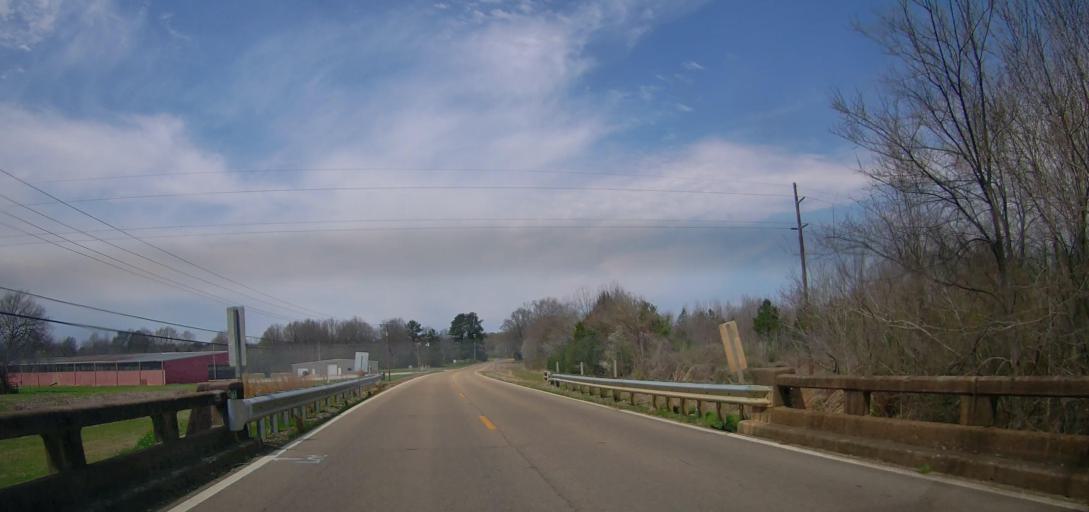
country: US
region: Mississippi
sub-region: Union County
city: New Albany
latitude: 34.4701
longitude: -88.9901
